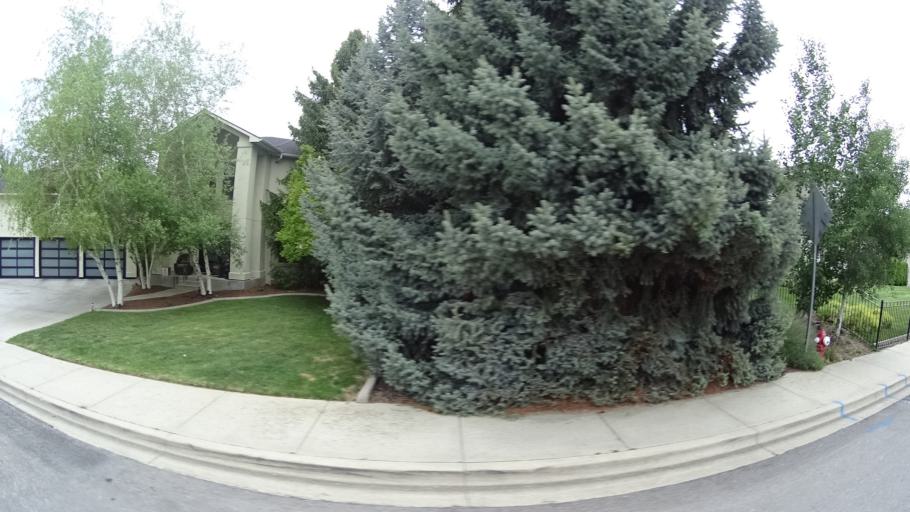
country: US
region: Idaho
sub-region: Ada County
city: Boise
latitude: 43.6148
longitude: -116.1604
